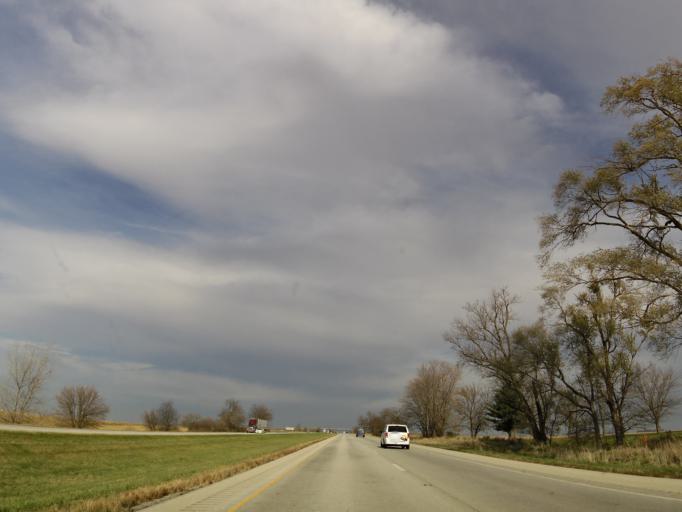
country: US
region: Illinois
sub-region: Knox County
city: Galesburg
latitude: 41.0164
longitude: -90.3347
